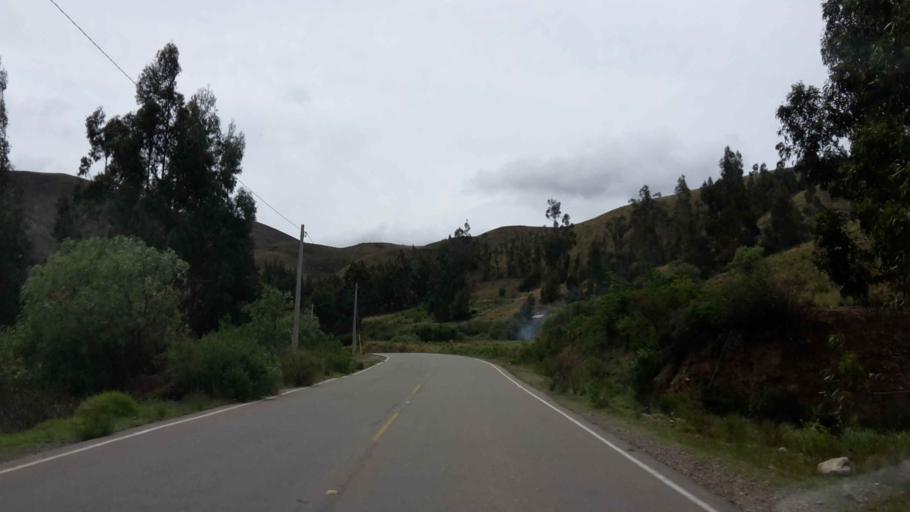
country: BO
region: Cochabamba
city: Colomi
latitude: -17.4094
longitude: -65.7785
